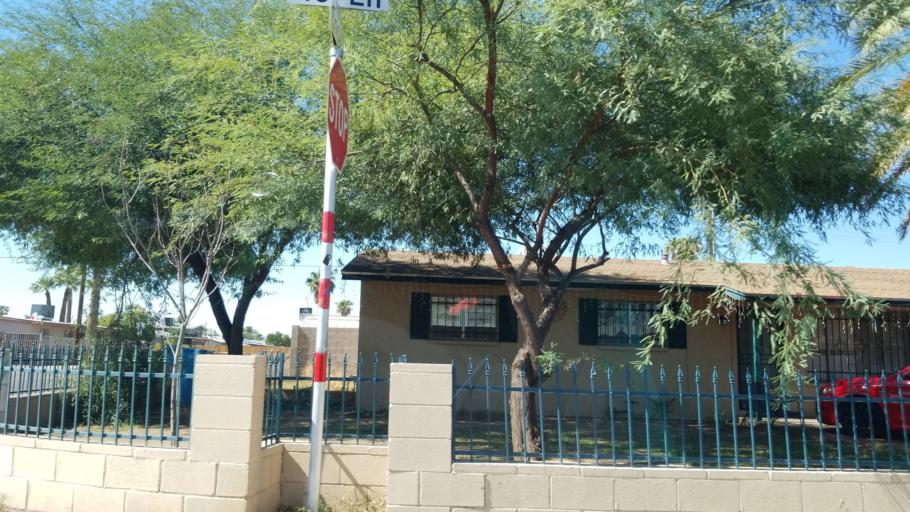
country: US
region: Arizona
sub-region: Maricopa County
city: Glendale
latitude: 33.4733
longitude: -112.1643
